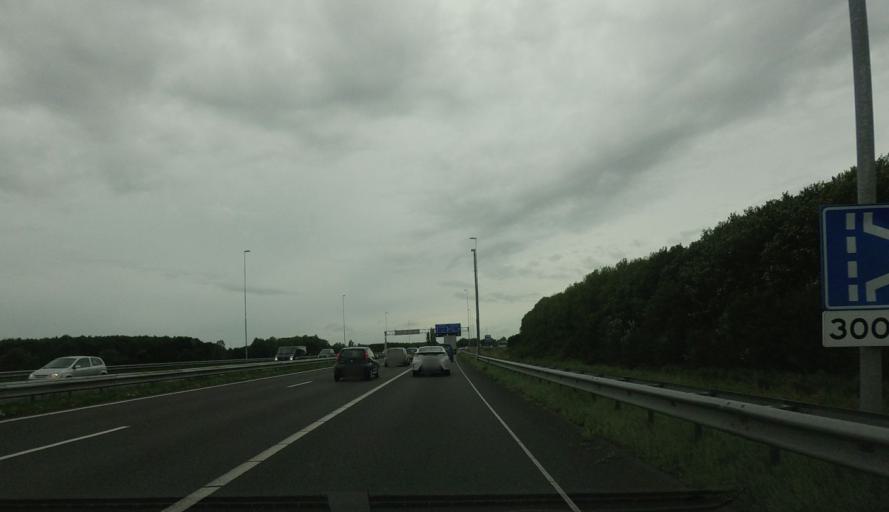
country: NL
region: North Holland
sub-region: Gemeente Velsen
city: Velsen-Zuid
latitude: 52.4246
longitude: 4.6860
